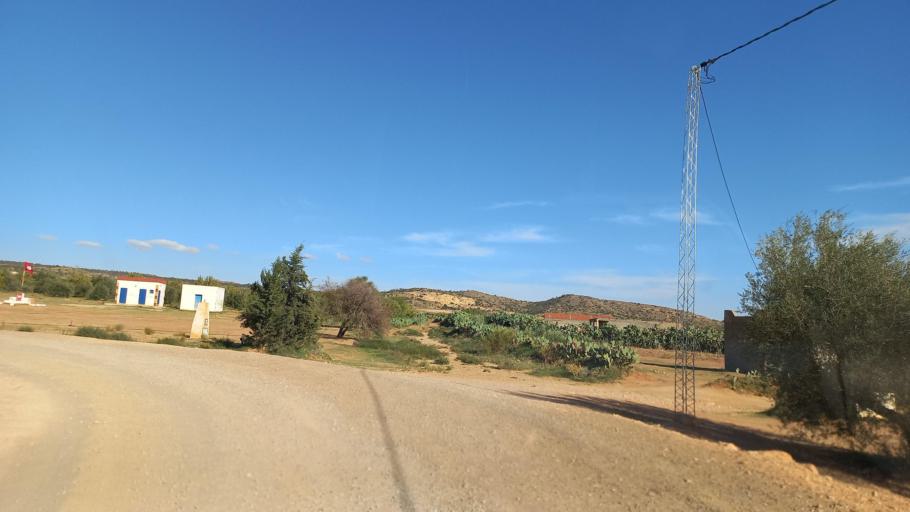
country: TN
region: Al Qasrayn
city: Sbiba
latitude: 35.2936
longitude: 9.1101
